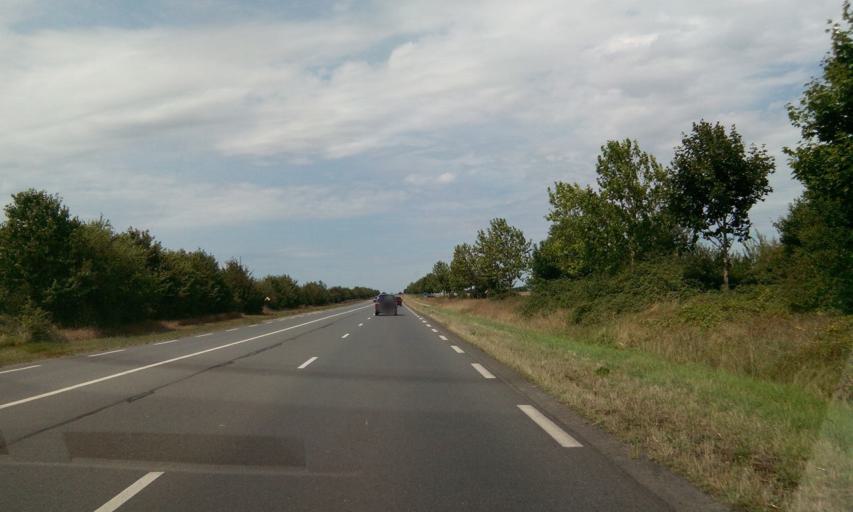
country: FR
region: Poitou-Charentes
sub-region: Departement des Deux-Sevres
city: Vouille
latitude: 46.3013
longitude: -0.3490
